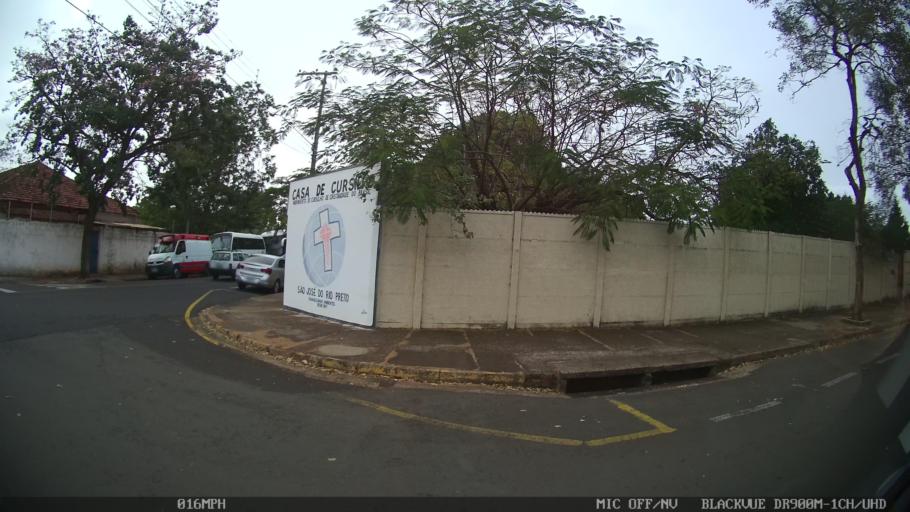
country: BR
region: Sao Paulo
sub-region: Sao Jose Do Rio Preto
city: Sao Jose do Rio Preto
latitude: -20.8319
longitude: -49.3960
